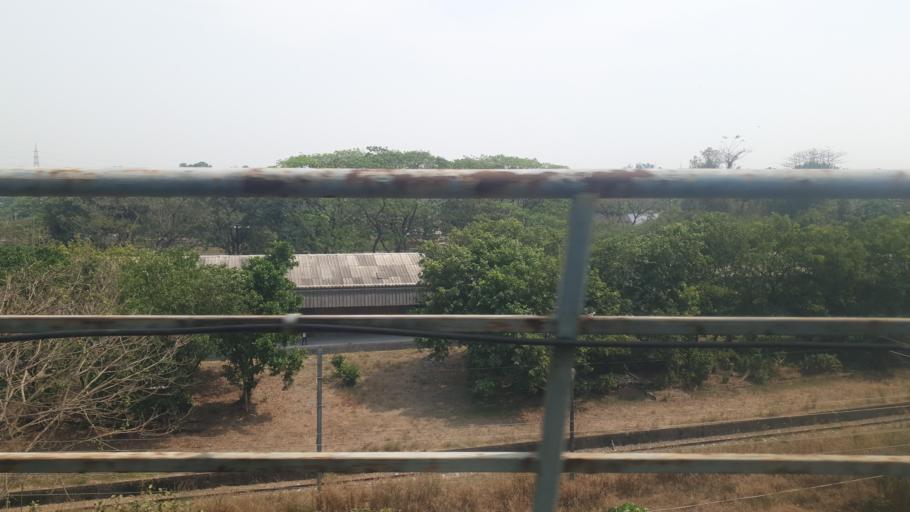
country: IN
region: Kerala
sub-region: Ernakulam
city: Elur
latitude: 10.0636
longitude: 76.3265
